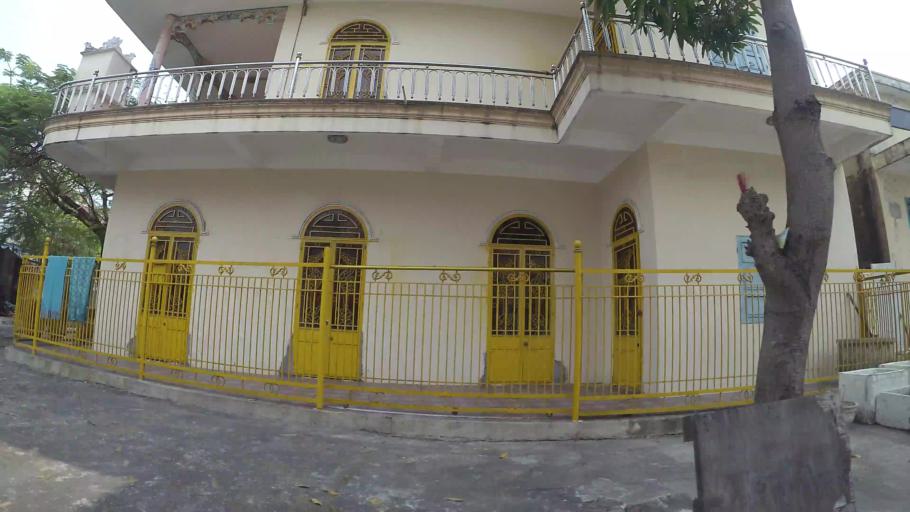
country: VN
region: Da Nang
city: Da Nang
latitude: 16.0848
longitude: 108.2307
